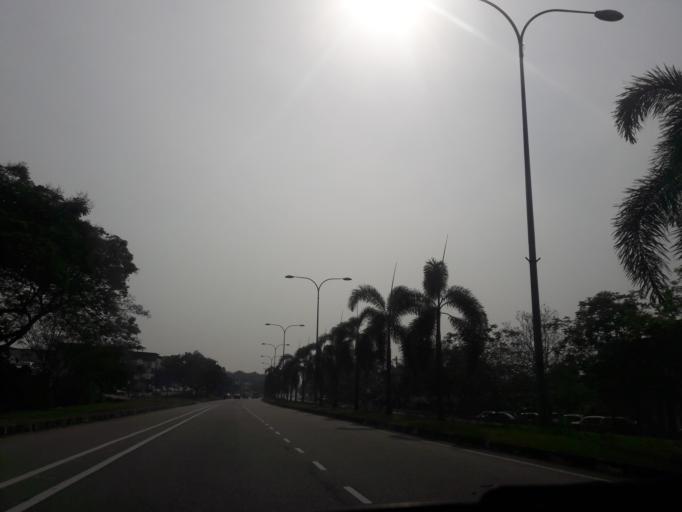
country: MY
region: Kedah
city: Kulim
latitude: 5.3512
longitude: 100.5287
